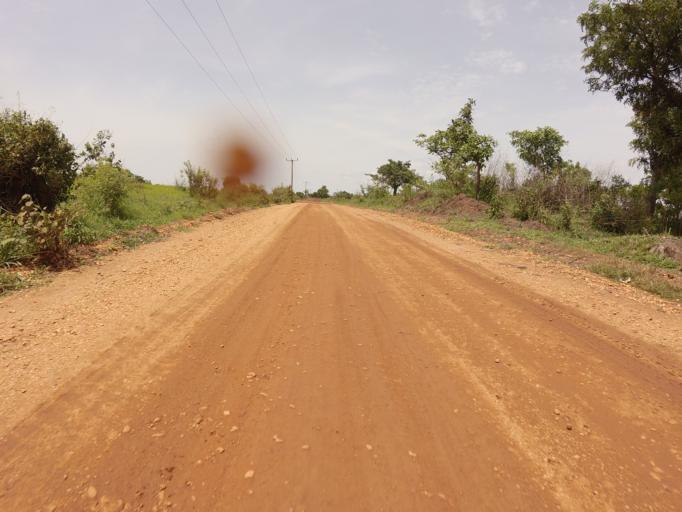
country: GH
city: Kpandae
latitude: 8.7130
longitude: 0.1469
